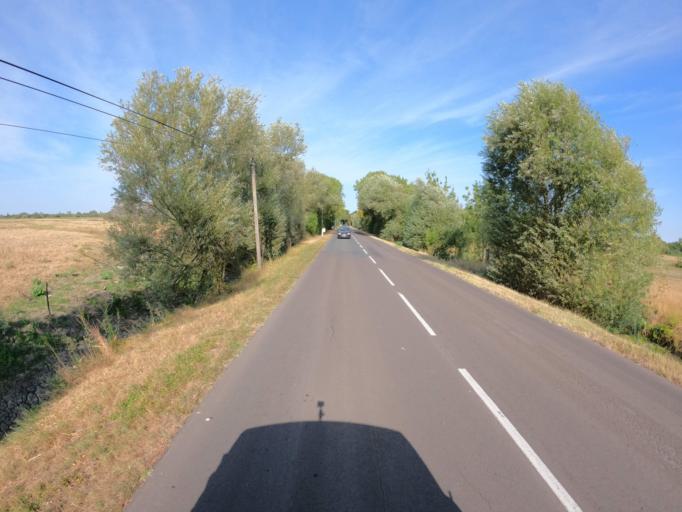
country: FR
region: Pays de la Loire
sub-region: Departement de la Vendee
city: Le Perrier
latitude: 46.8045
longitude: -1.9700
